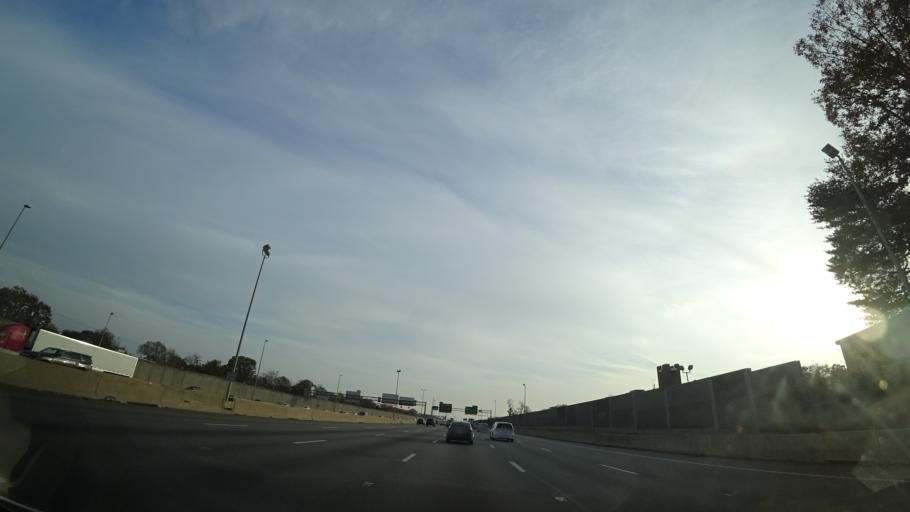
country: US
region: Virginia
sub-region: Fairfax County
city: Springfield
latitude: 38.7665
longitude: -77.1834
